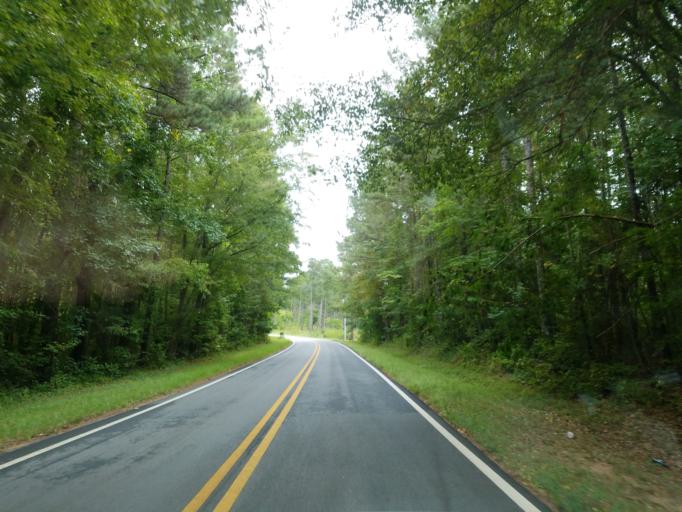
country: US
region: Georgia
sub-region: Monroe County
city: Forsyth
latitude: 32.9096
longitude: -83.8943
